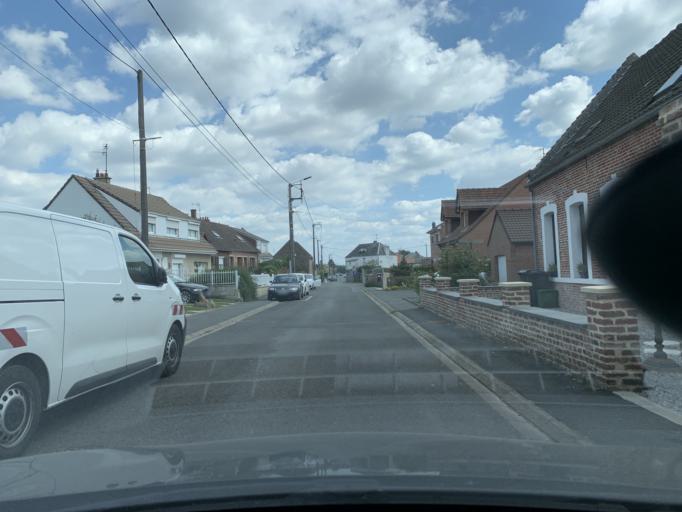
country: FR
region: Nord-Pas-de-Calais
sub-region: Departement du Pas-de-Calais
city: Ecourt-Saint-Quentin
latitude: 50.2533
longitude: 3.0746
